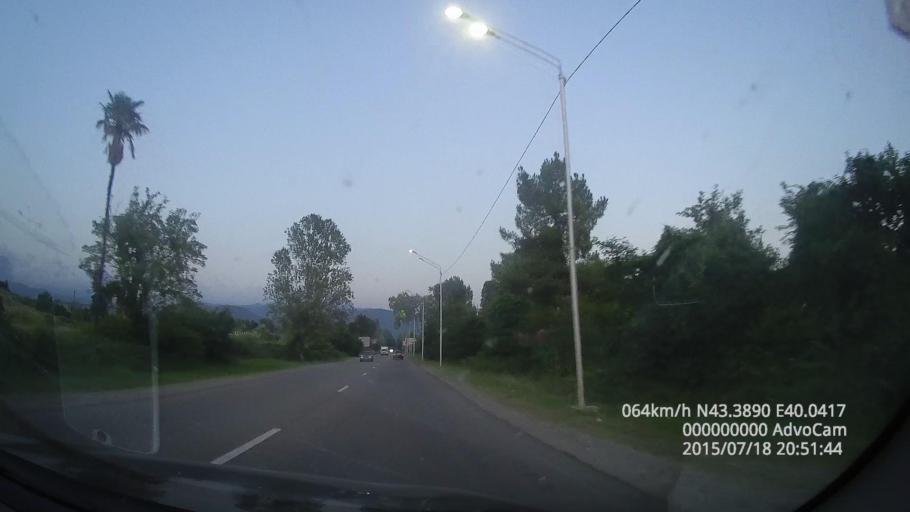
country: GE
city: Gantiadi
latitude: 43.3888
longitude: 40.0432
